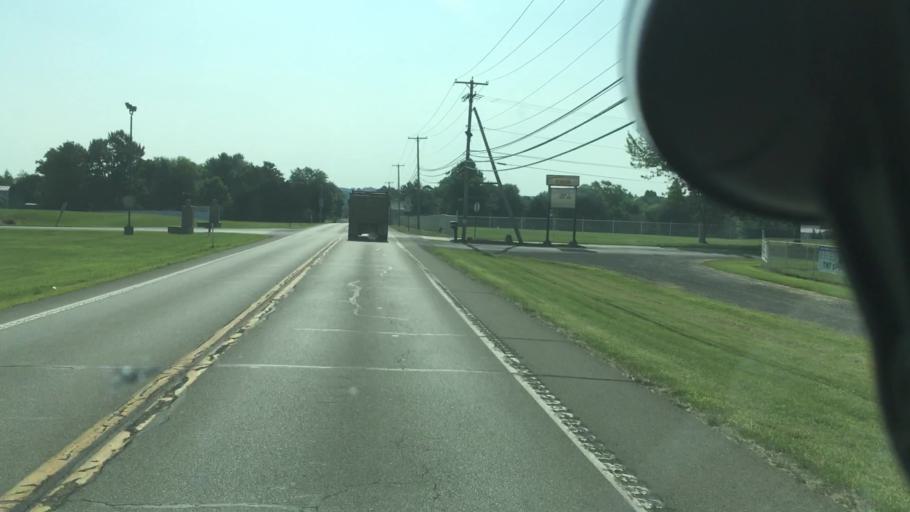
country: US
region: Pennsylvania
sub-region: Lawrence County
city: New Castle
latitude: 41.0132
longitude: -80.2603
